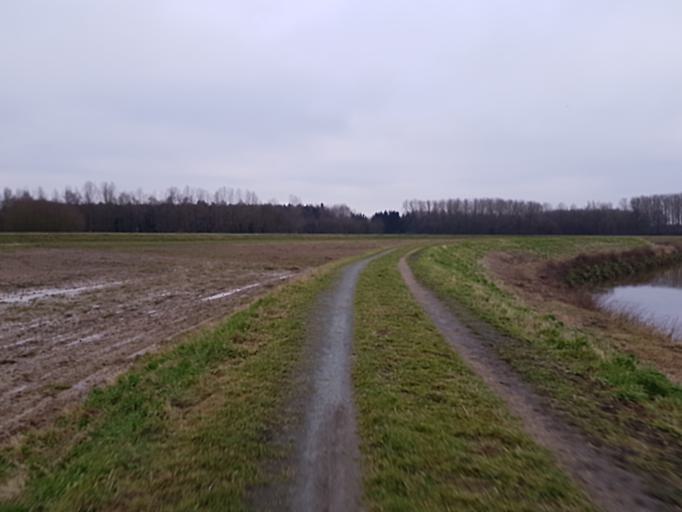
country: BE
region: Flanders
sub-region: Provincie Vlaams-Brabant
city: Tremelo
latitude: 50.9827
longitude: 4.6775
